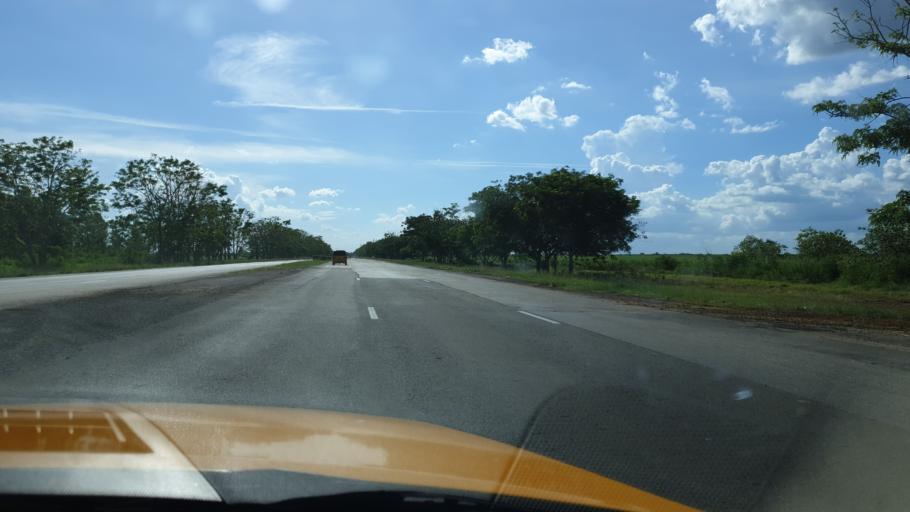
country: CU
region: Cienfuegos
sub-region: Municipio de Aguada de Pasajeros
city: Aguada de Pasajeros
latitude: 22.4112
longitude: -80.8945
